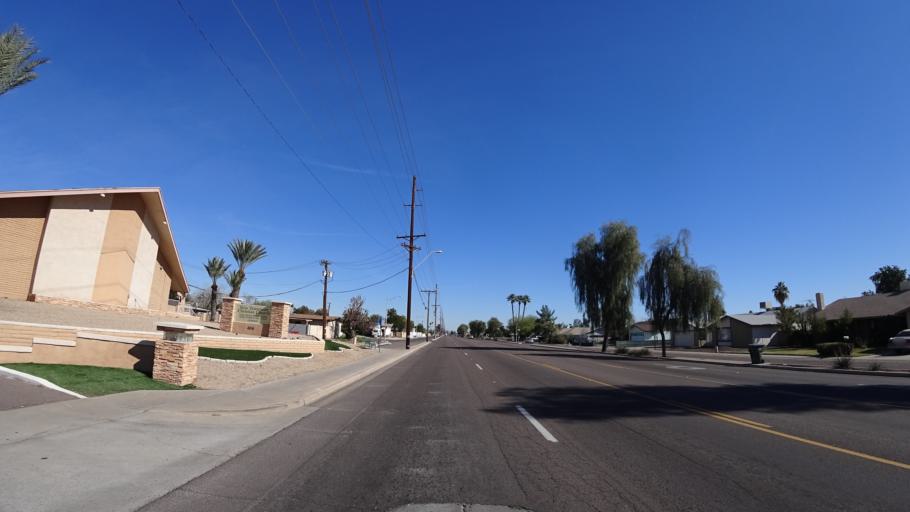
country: US
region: Arizona
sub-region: Maricopa County
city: Glendale
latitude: 33.5095
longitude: -112.2004
